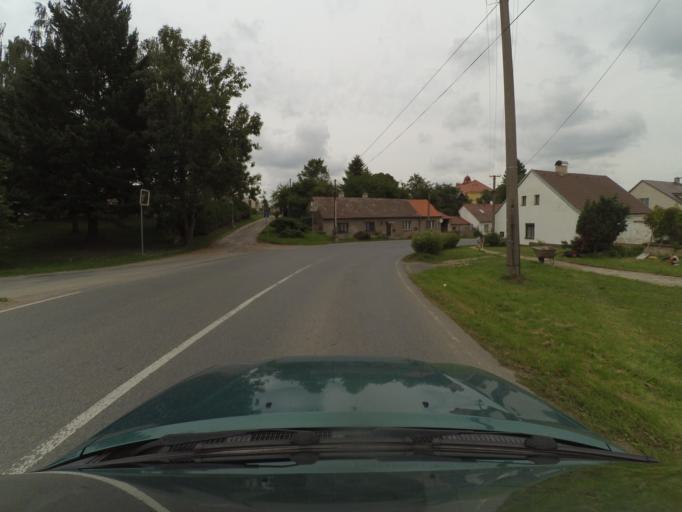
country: CZ
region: Plzensky
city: Kozlany
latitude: 50.0275
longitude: 13.5670
